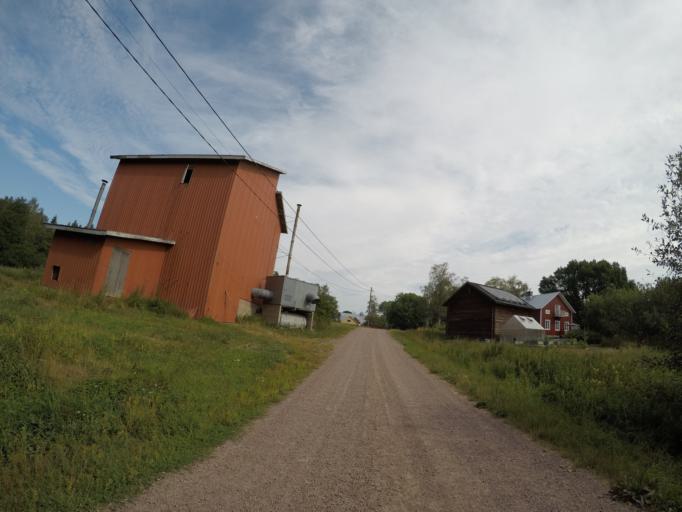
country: AX
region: Alands landsbygd
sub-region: Finstroem
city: Finstroem
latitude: 60.2272
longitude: 19.8500
